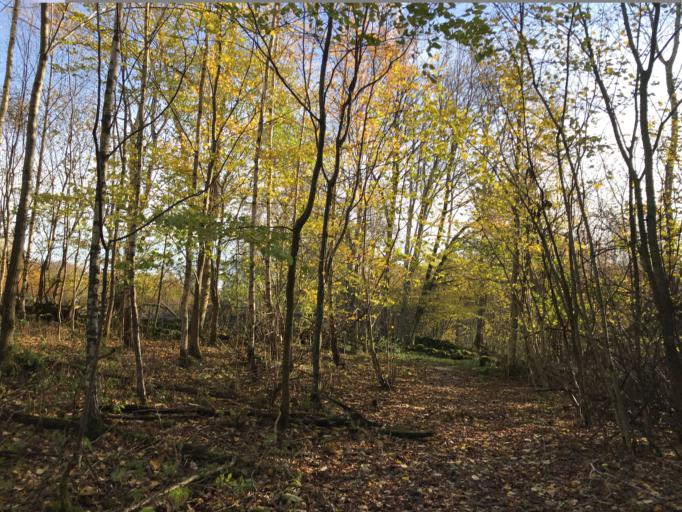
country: SE
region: Skane
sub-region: Svalovs Kommun
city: Kagerod
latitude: 56.0268
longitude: 13.1023
